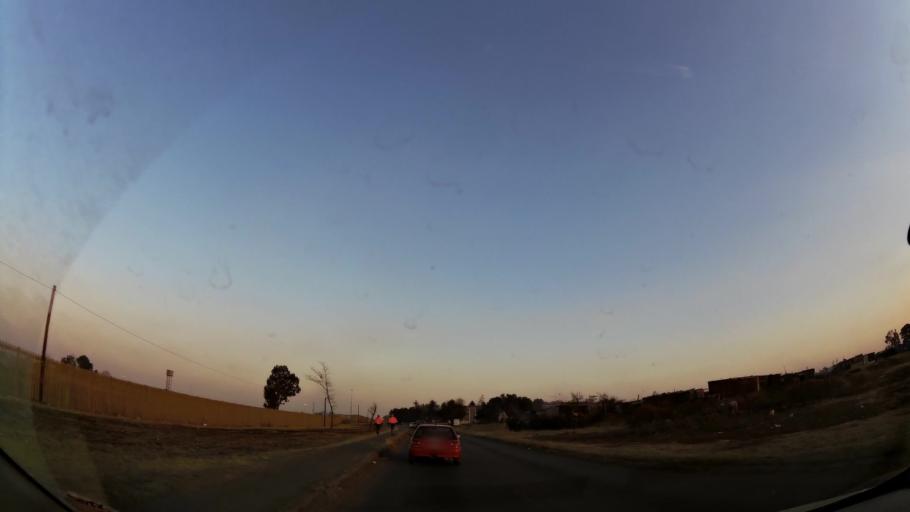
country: ZA
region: Gauteng
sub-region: Ekurhuleni Metropolitan Municipality
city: Springs
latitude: -26.2861
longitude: 28.4046
